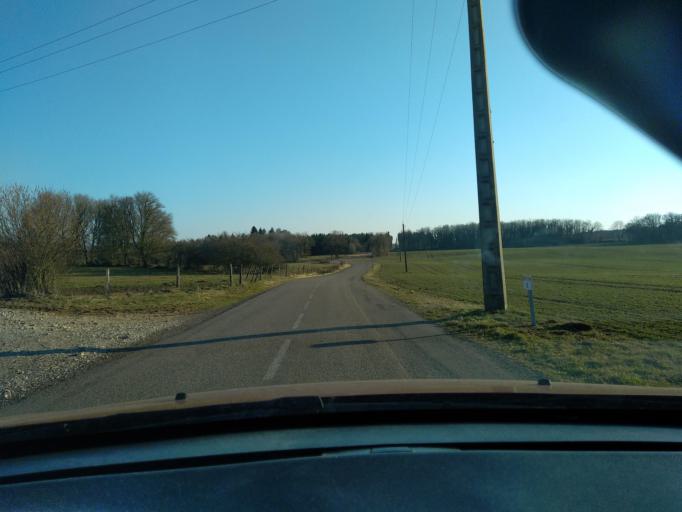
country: FR
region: Franche-Comte
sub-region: Departement du Jura
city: Perrigny
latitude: 46.6576
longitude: 5.6445
